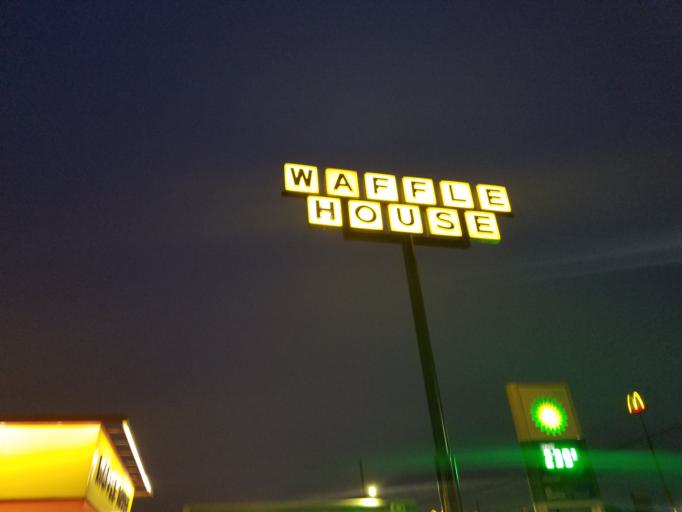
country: US
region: Georgia
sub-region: Tift County
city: Tifton
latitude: 31.4583
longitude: -83.5278
